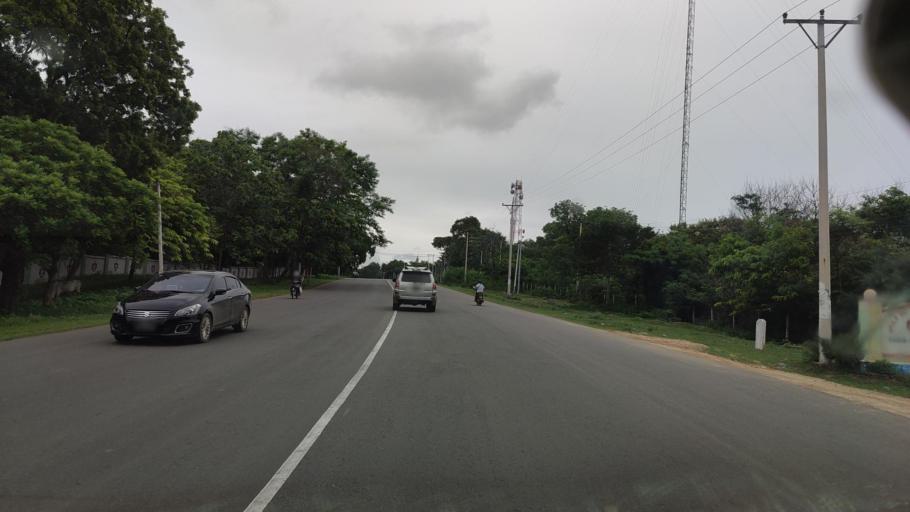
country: MM
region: Mandalay
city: Meiktila
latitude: 20.8674
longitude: 95.8684
